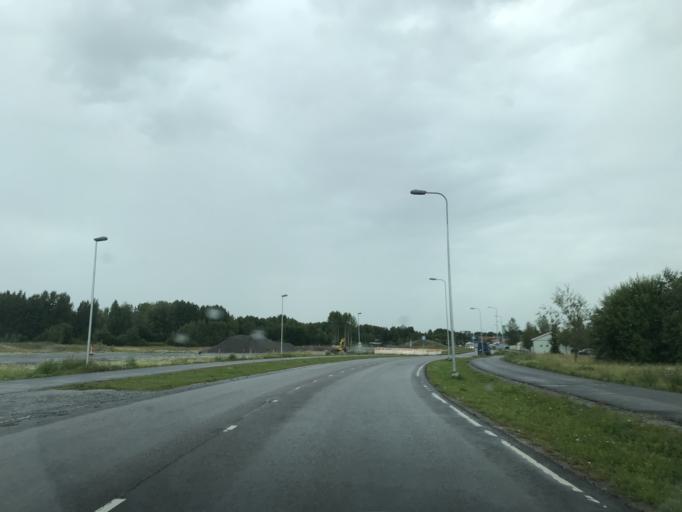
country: FI
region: Uusimaa
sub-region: Helsinki
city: Vihti
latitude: 60.3235
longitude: 24.3155
